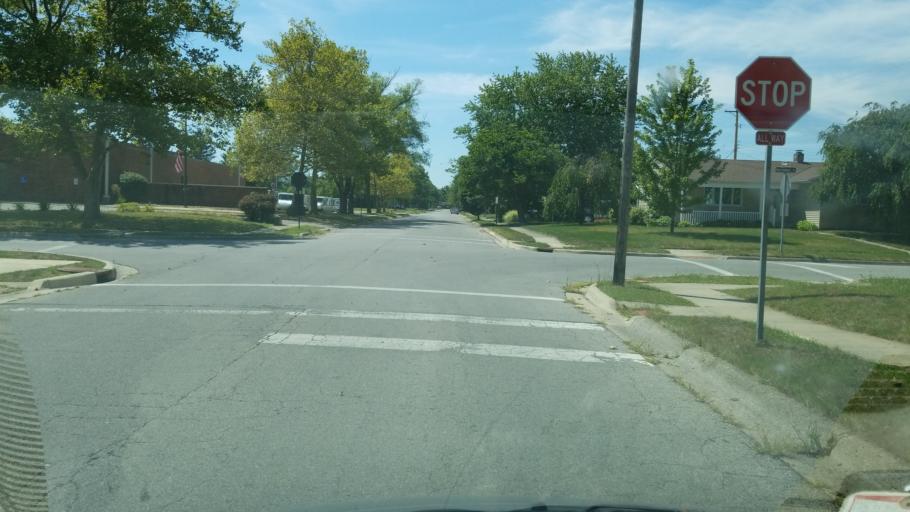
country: US
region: Ohio
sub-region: Franklin County
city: Grove City
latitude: 39.8798
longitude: -83.0712
